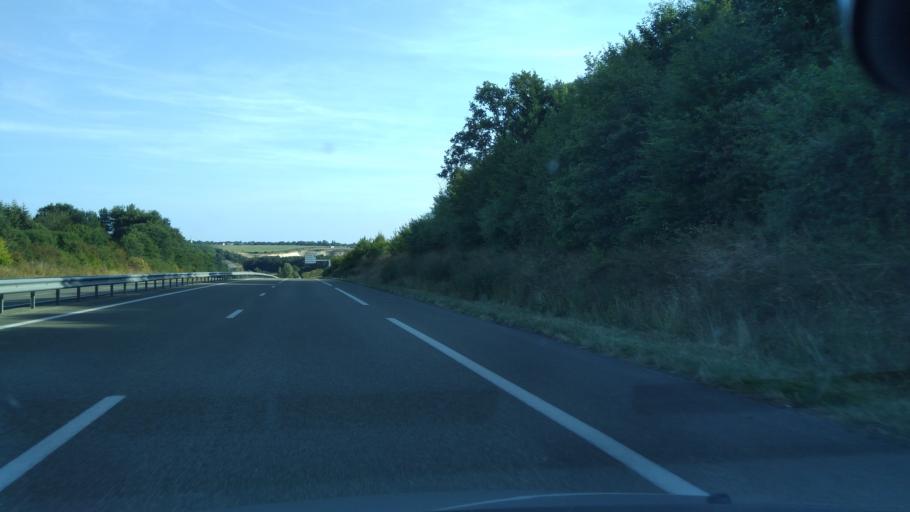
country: FR
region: Pays de la Loire
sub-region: Departement de la Mayenne
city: Entrammes
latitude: 48.0071
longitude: -0.7267
